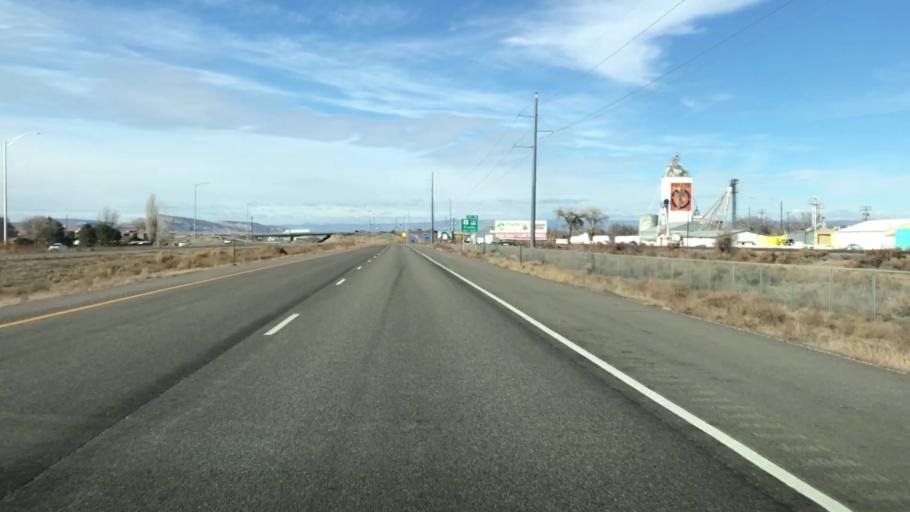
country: US
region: Colorado
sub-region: Mesa County
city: Fruita
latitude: 39.1525
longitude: -108.7296
